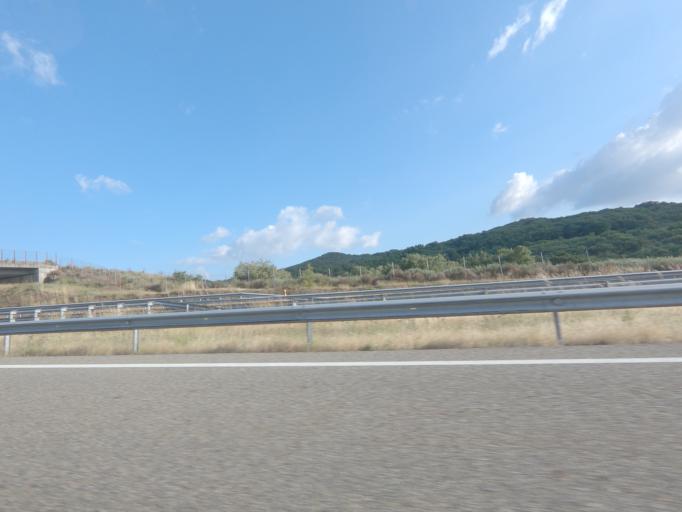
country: ES
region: Galicia
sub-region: Provincia de Ourense
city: Cualedro
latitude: 42.0104
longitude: -7.5782
